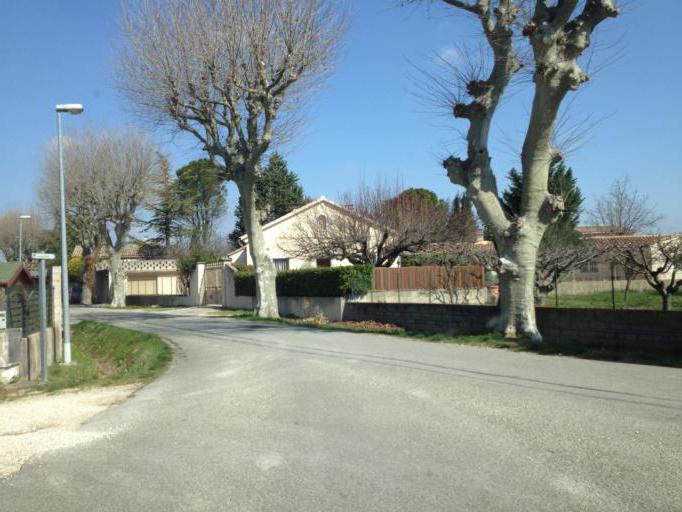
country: FR
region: Provence-Alpes-Cote d'Azur
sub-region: Departement du Vaucluse
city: Jonquieres
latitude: 44.1104
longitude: 4.9023
